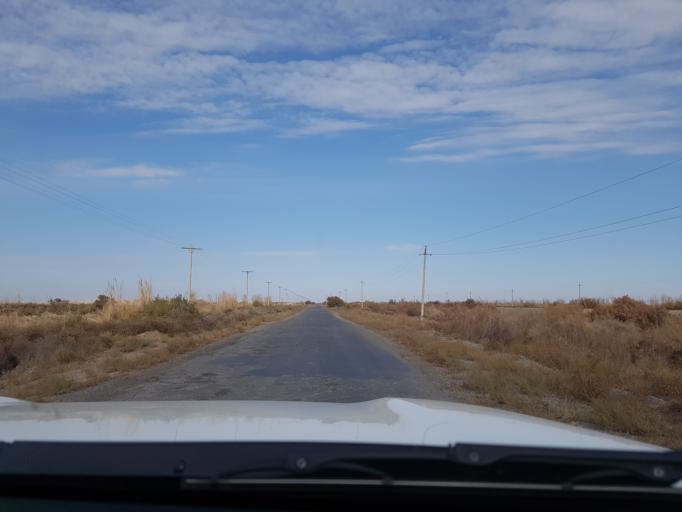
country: TM
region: Ahal
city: Tejen
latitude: 37.4019
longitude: 61.0957
